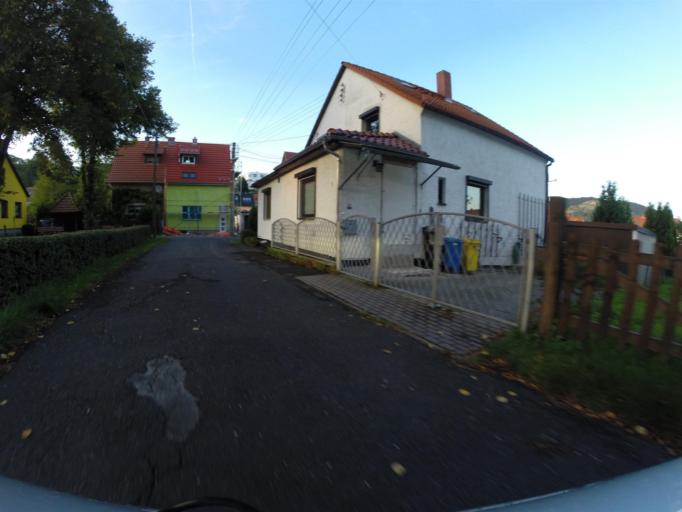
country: DE
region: Thuringia
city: Jena
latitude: 50.9060
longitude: 11.5728
